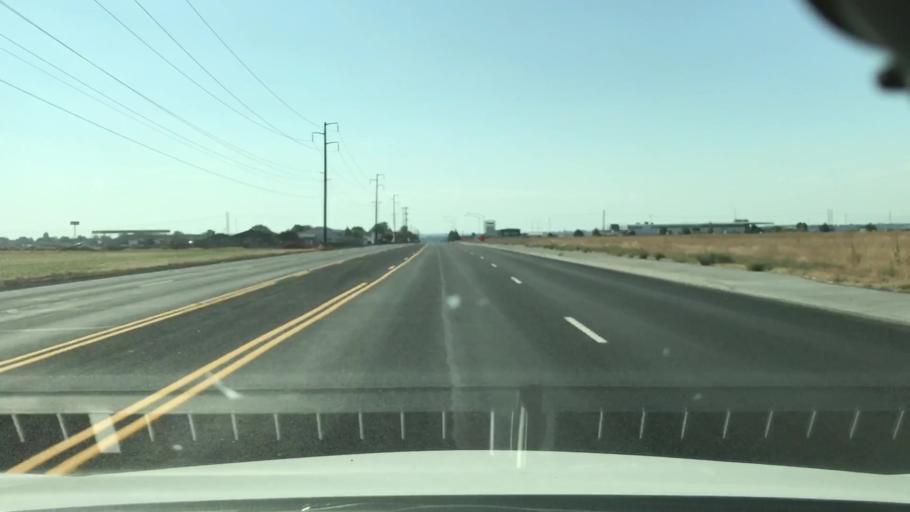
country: US
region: Washington
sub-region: Grant County
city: Moses Lake
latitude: 47.1310
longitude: -119.2443
